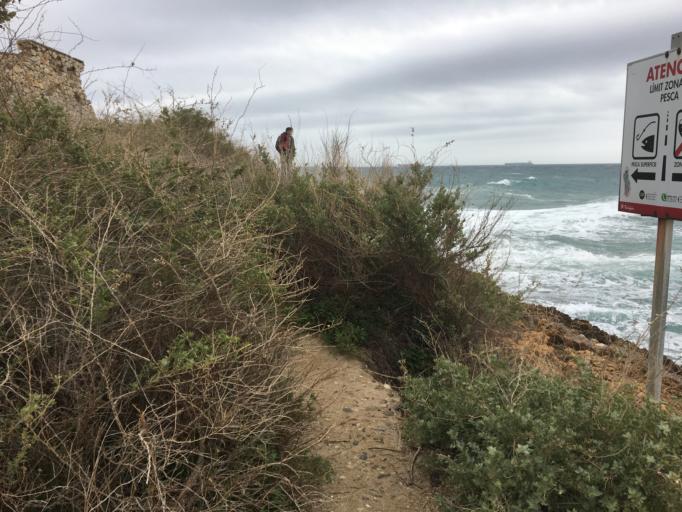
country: ES
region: Catalonia
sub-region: Provincia de Tarragona
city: Tarragona
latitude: 41.1129
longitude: 1.2660
